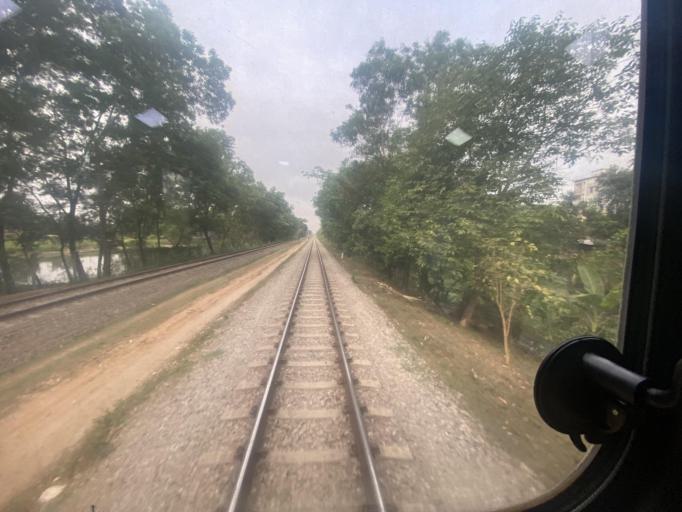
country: BD
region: Dhaka
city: Tungi
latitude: 23.9199
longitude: 90.4363
